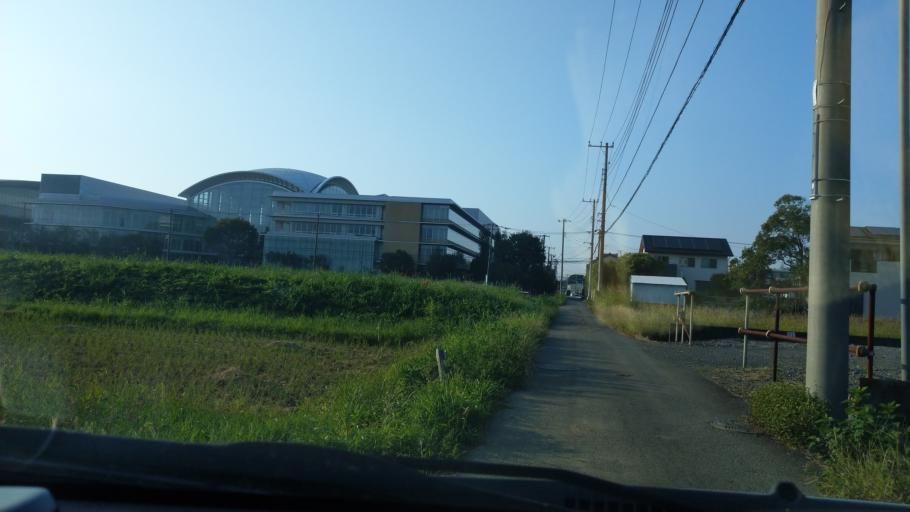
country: JP
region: Saitama
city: Yono
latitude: 35.8550
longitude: 139.6119
